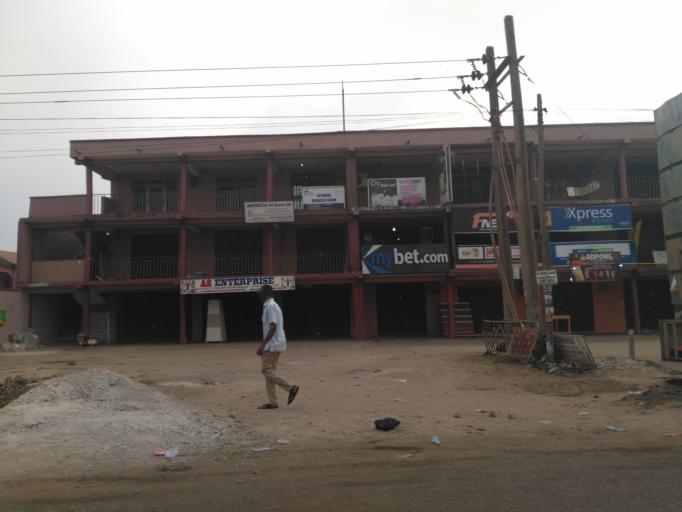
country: GH
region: Ashanti
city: Tafo
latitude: 6.7105
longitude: -1.5993
